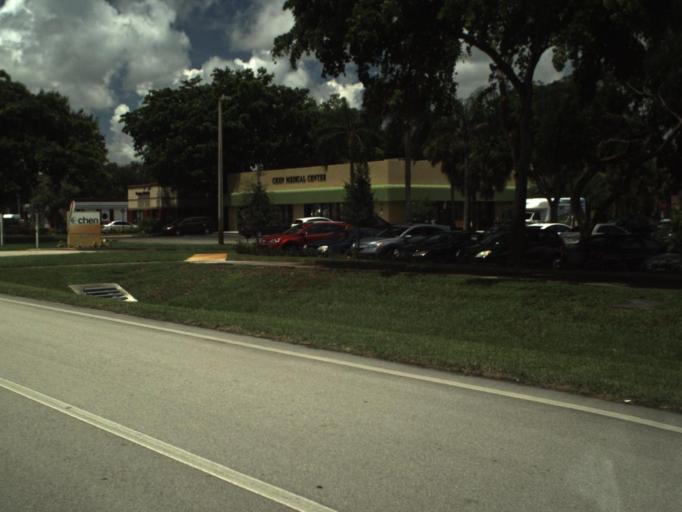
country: US
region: Florida
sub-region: Broward County
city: Miramar
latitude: 26.0091
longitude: -80.2564
